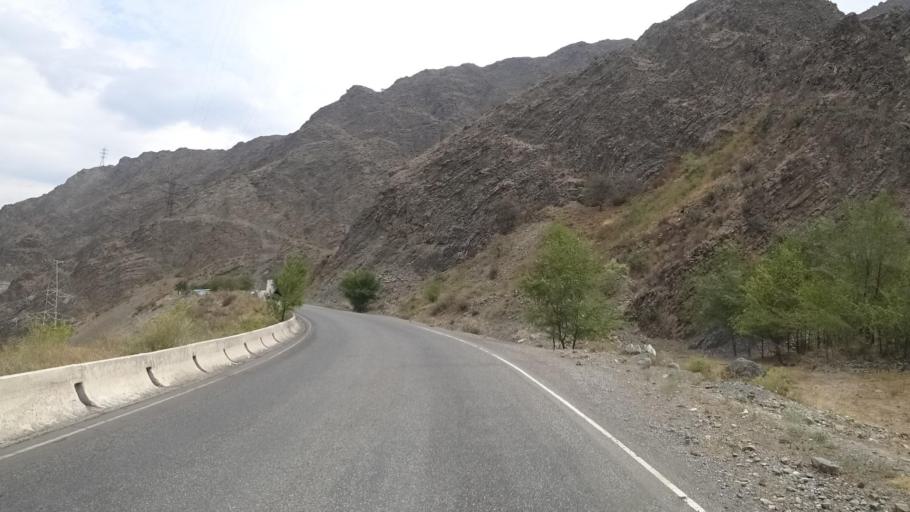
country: KG
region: Jalal-Abad
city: Tash-Kumyr
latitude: 41.4940
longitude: 72.3621
